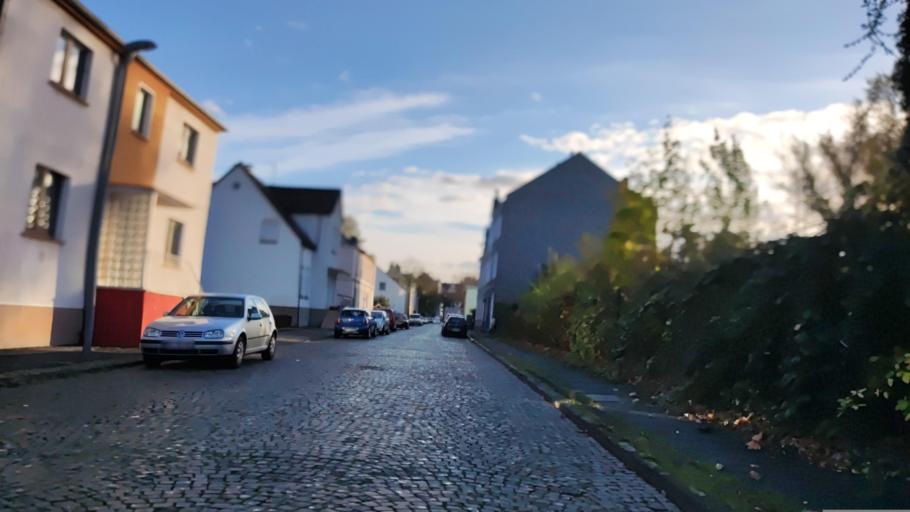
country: DE
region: North Rhine-Westphalia
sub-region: Regierungsbezirk Arnsberg
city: Bochum
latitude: 51.5061
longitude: 7.2075
